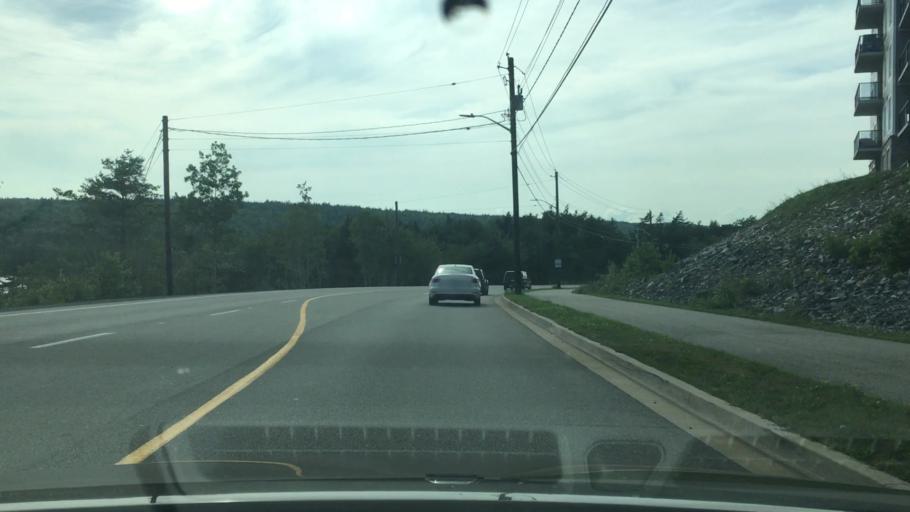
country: CA
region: Nova Scotia
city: Dartmouth
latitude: 44.6997
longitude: -63.6983
